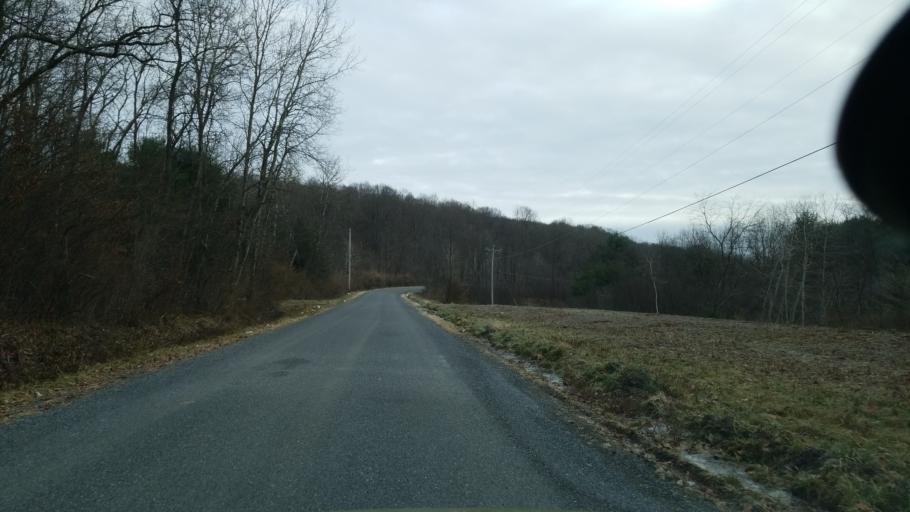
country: US
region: Pennsylvania
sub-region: Clearfield County
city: Treasure Lake
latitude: 41.1388
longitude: -78.6014
